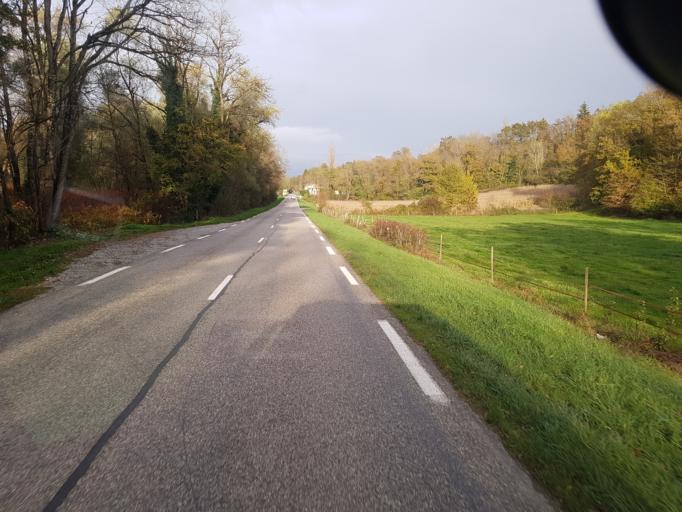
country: FR
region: Rhone-Alpes
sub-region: Departement de la Haute-Savoie
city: Frangy
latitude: 45.9995
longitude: 5.8564
